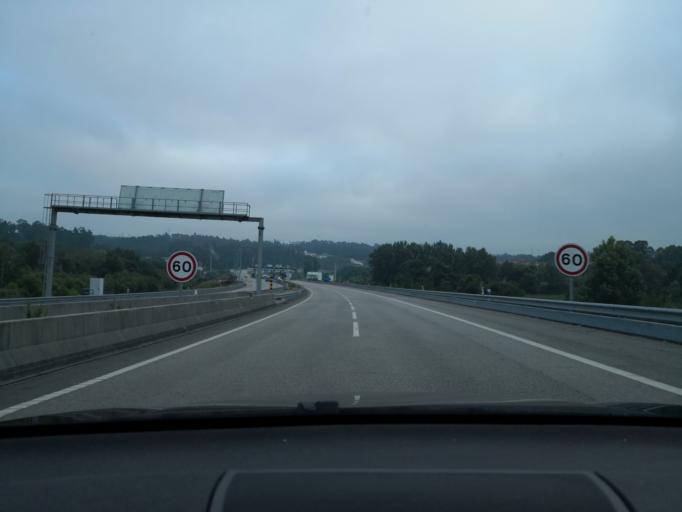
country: PT
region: Aveiro
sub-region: Santa Maria da Feira
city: Argoncilhe
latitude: 41.0175
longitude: -8.5278
